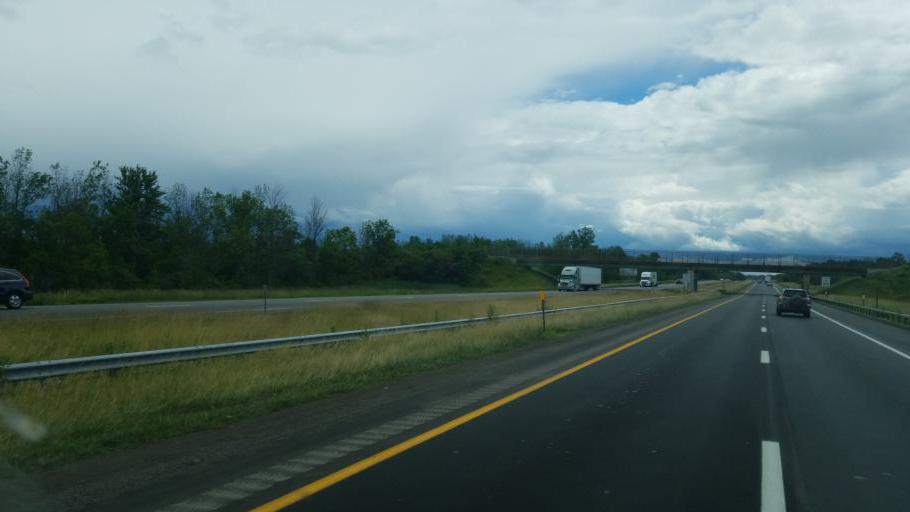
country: US
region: New York
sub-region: Livingston County
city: Caledonia
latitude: 43.0299
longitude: -77.8794
